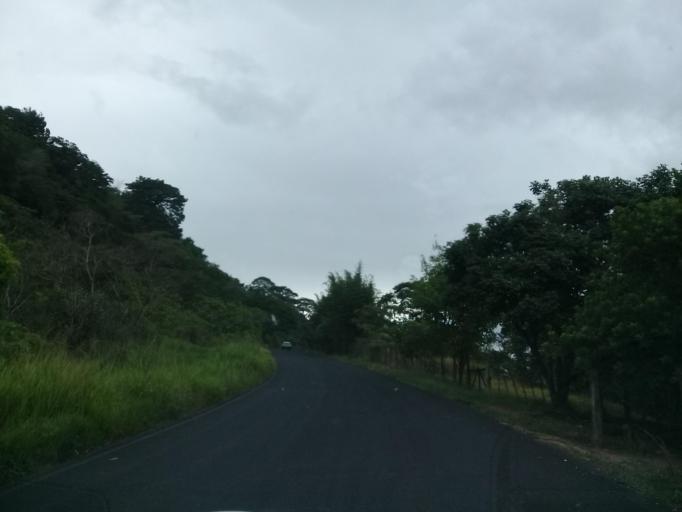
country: MX
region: Veracruz
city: El Castillo
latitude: 19.5603
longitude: -96.8459
